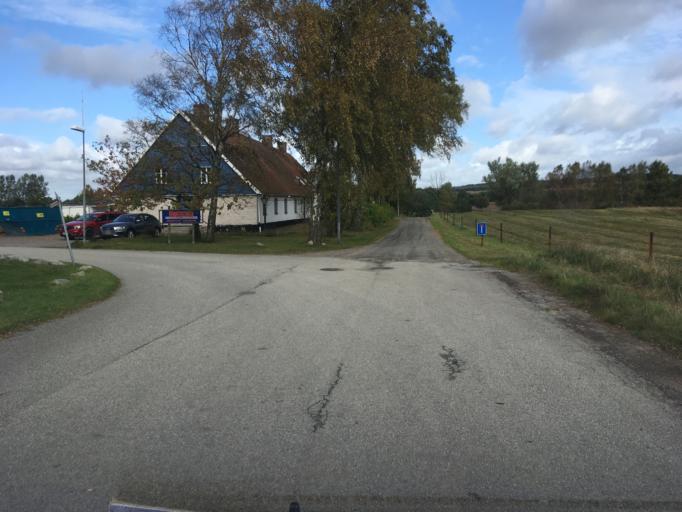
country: SE
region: Skane
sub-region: Lunds Kommun
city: Genarp
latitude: 55.5995
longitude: 13.4116
